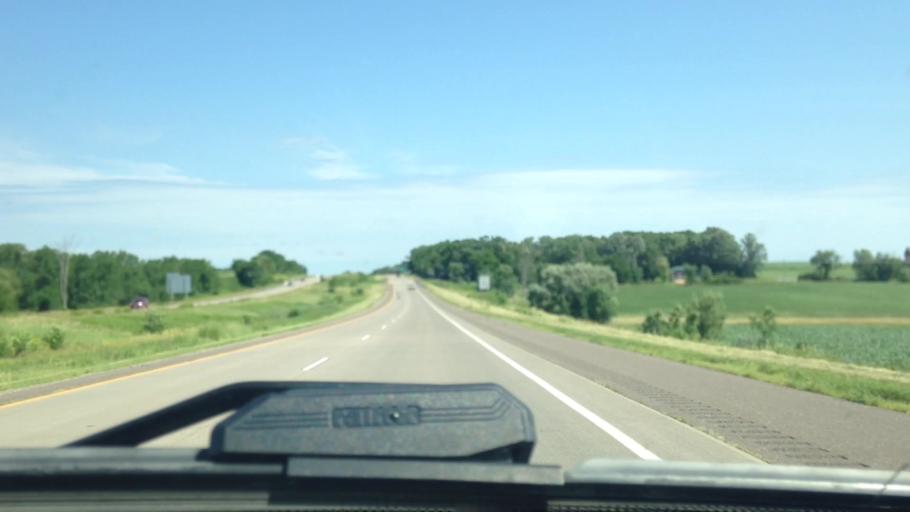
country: US
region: Wisconsin
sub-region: Barron County
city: Rice Lake
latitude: 45.5269
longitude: -91.7594
